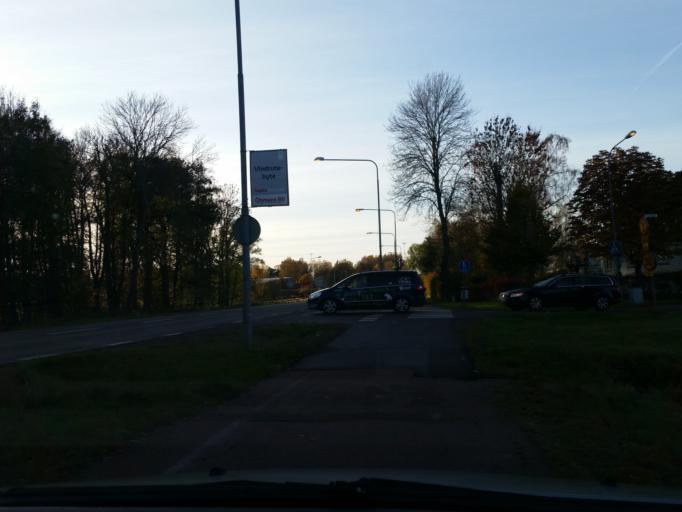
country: AX
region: Mariehamns stad
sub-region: Mariehamn
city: Mariehamn
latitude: 60.1149
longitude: 19.9466
